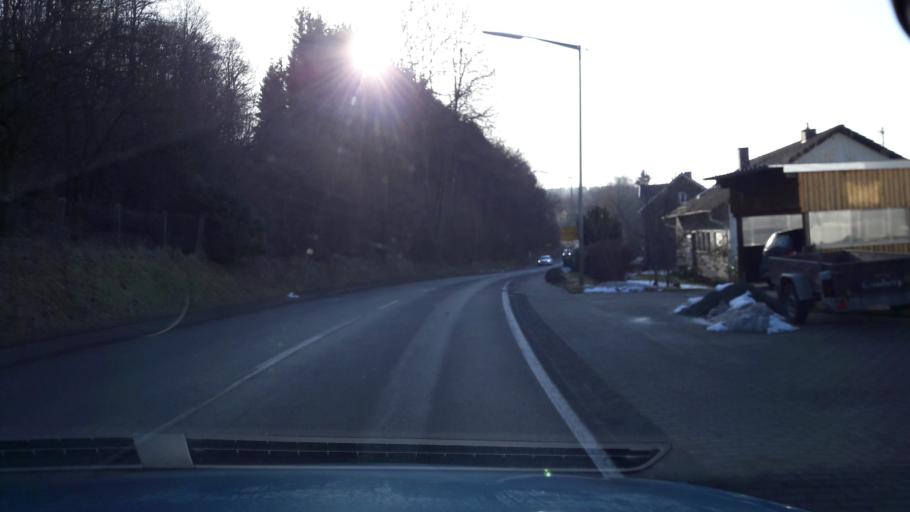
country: DE
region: North Rhine-Westphalia
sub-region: Regierungsbezirk Arnsberg
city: Wilnsdorf
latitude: 50.8066
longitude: 8.0887
